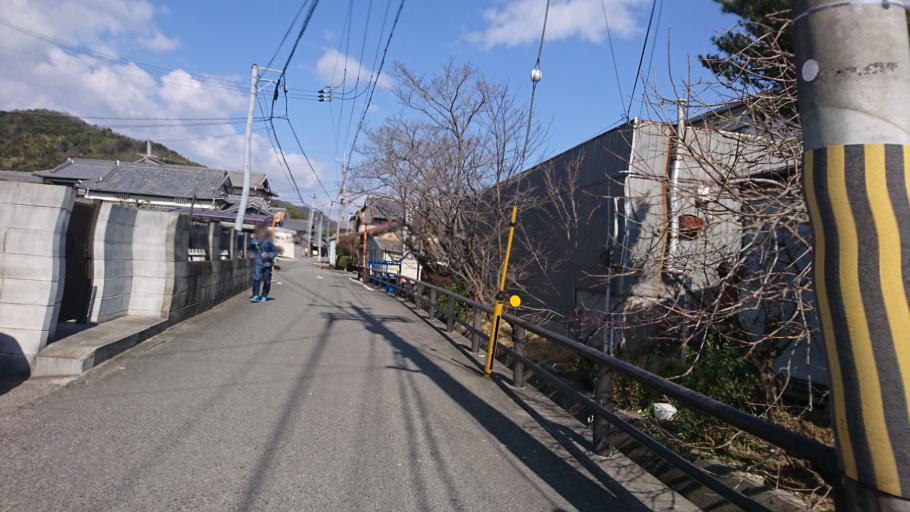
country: JP
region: Hyogo
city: Kakogawacho-honmachi
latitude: 34.8125
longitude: 134.8045
